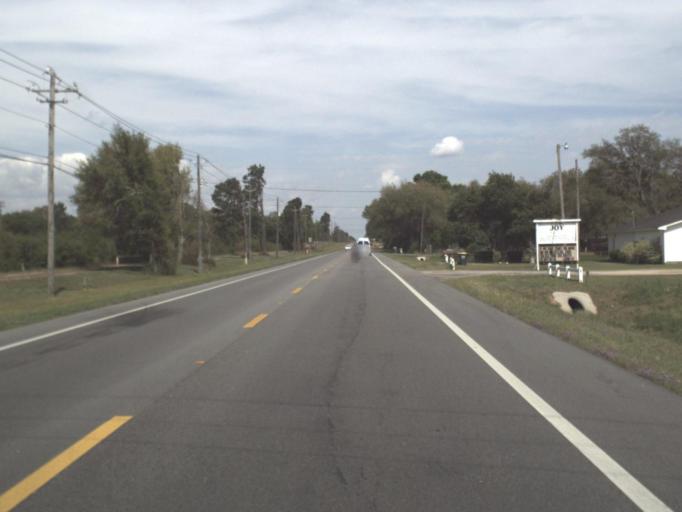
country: US
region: Florida
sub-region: Santa Rosa County
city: East Milton
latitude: 30.6370
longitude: -86.9629
